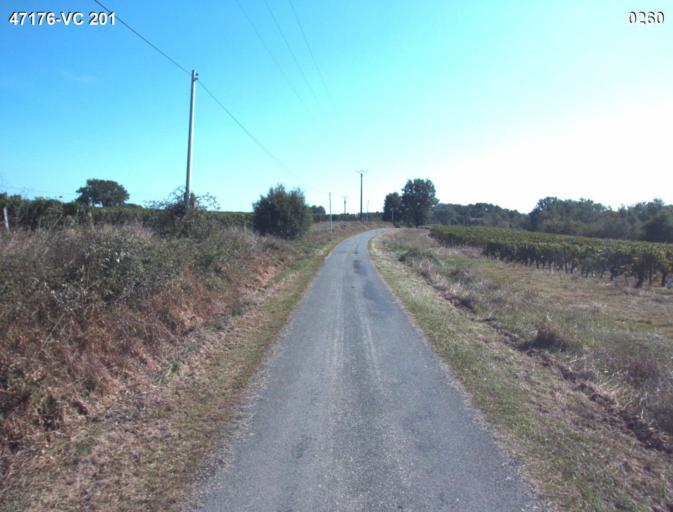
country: FR
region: Aquitaine
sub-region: Departement du Lot-et-Garonne
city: Vianne
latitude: 44.2105
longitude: 0.3108
